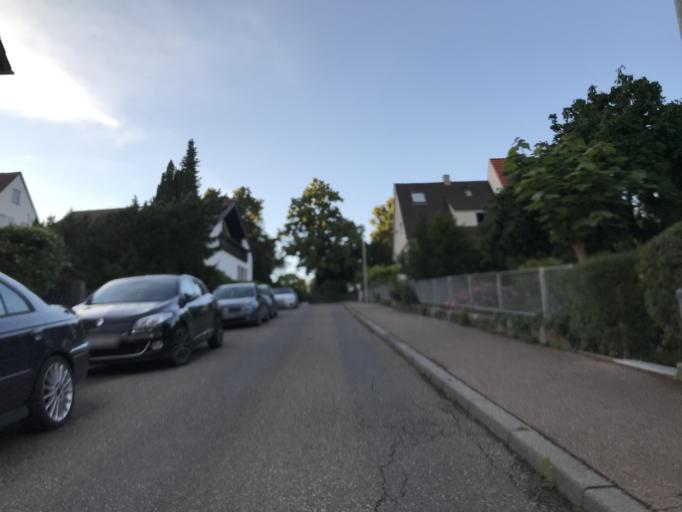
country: DE
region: Baden-Wuerttemberg
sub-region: Regierungsbezirk Stuttgart
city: Korntal
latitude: 48.8151
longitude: 9.1172
